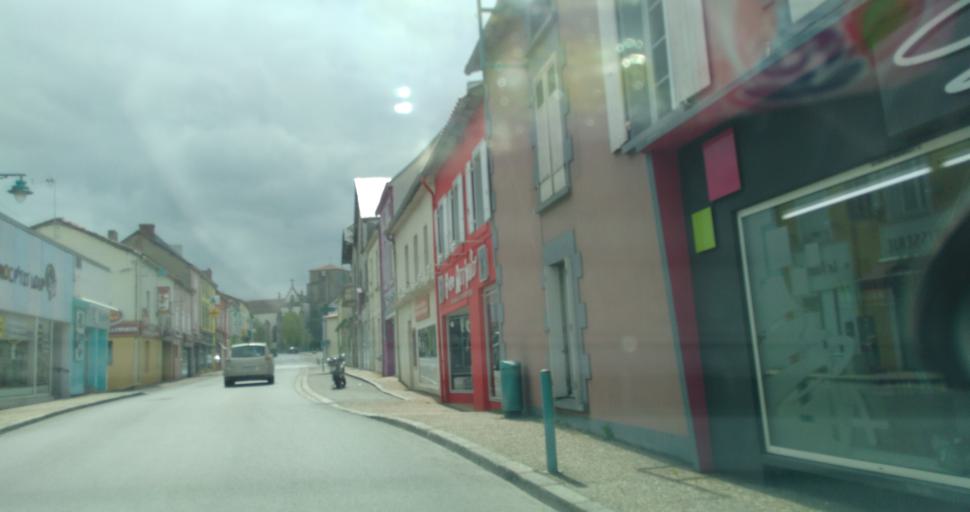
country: FR
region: Poitou-Charentes
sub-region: Departement des Deux-Sevres
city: Moncoutant
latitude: 46.7245
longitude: -0.5883
